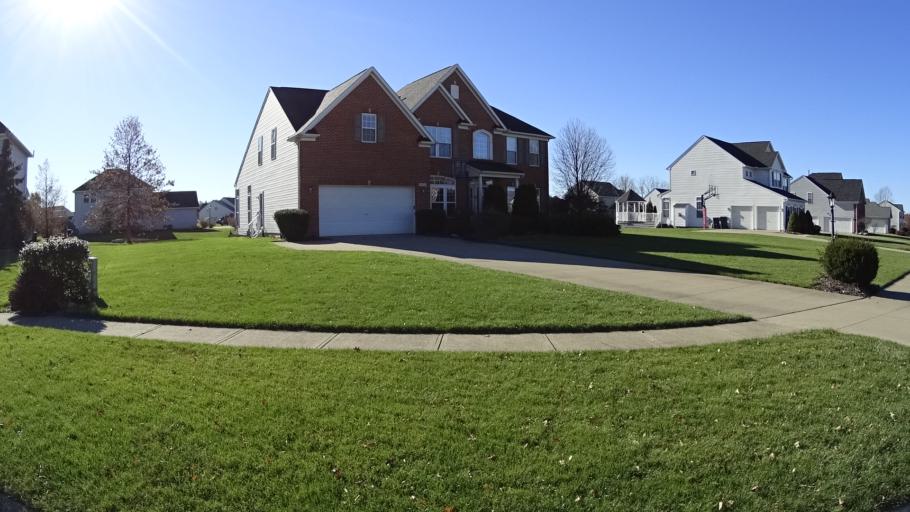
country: US
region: Ohio
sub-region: Lorain County
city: Avon
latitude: 41.4230
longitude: -82.0566
